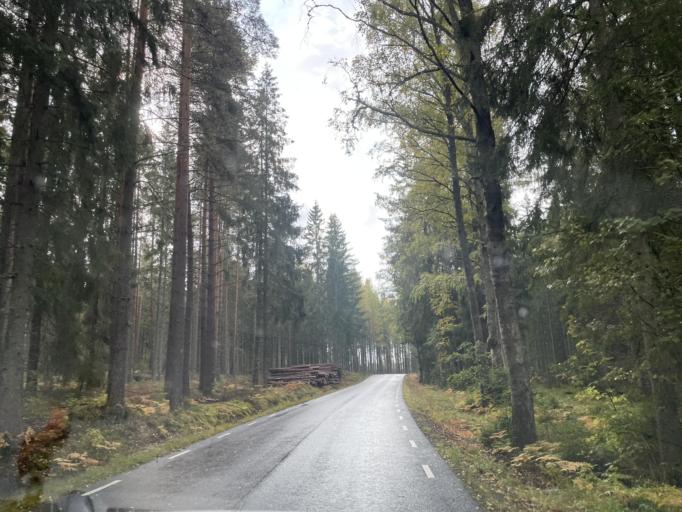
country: SE
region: Vaermland
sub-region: Karlstads Kommun
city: Skattkarr
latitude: 59.4338
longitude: 13.6075
